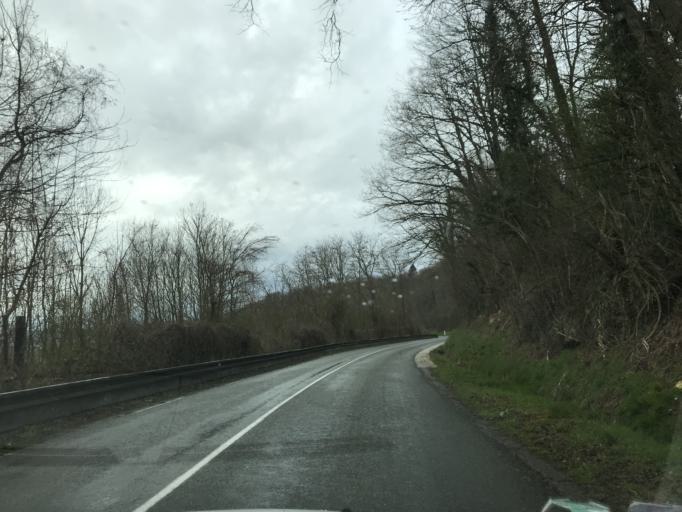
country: FR
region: Picardie
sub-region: Departement de l'Aisne
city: Belleu
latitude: 49.3582
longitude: 3.3520
